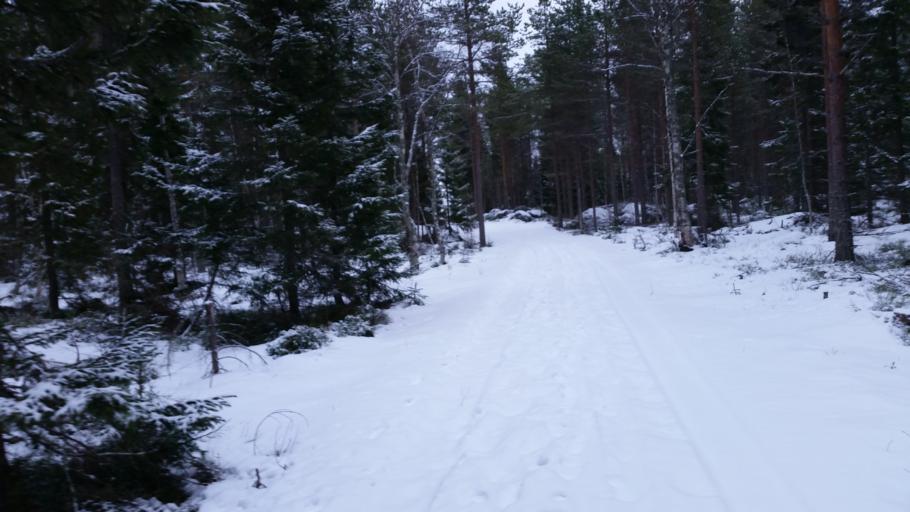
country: SE
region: Vaesterbotten
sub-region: Umea Kommun
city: Saevar
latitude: 63.9148
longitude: 20.7930
